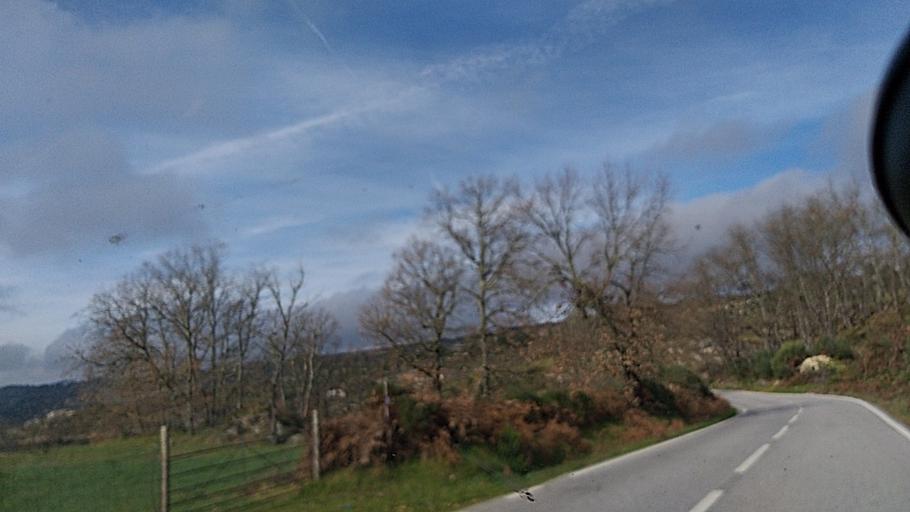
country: PT
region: Guarda
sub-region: Aguiar da Beira
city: Aguiar da Beira
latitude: 40.7471
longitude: -7.5517
